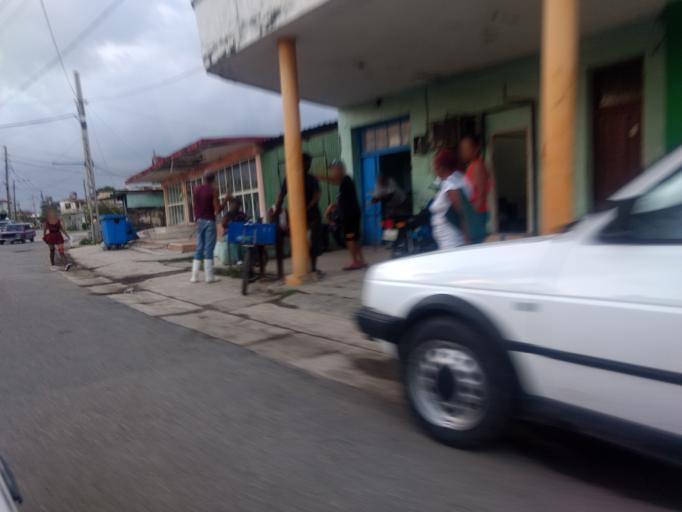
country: CU
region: Artemisa
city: Bauta
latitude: 23.0787
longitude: -82.5113
